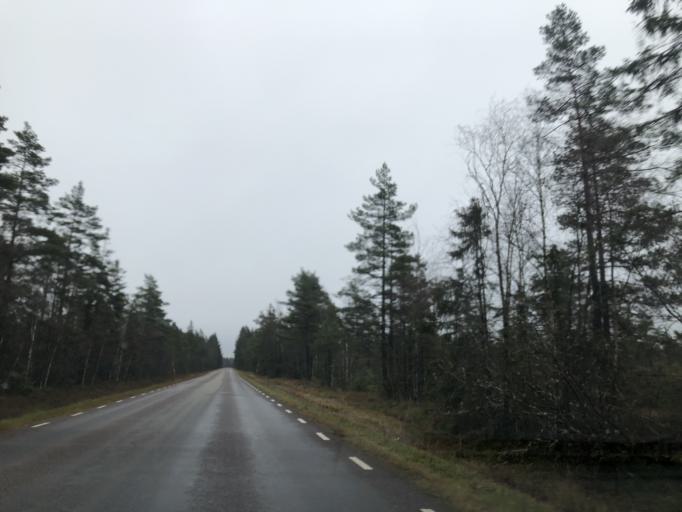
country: SE
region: Vaestra Goetaland
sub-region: Ulricehamns Kommun
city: Ulricehamn
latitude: 57.7594
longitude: 13.4918
